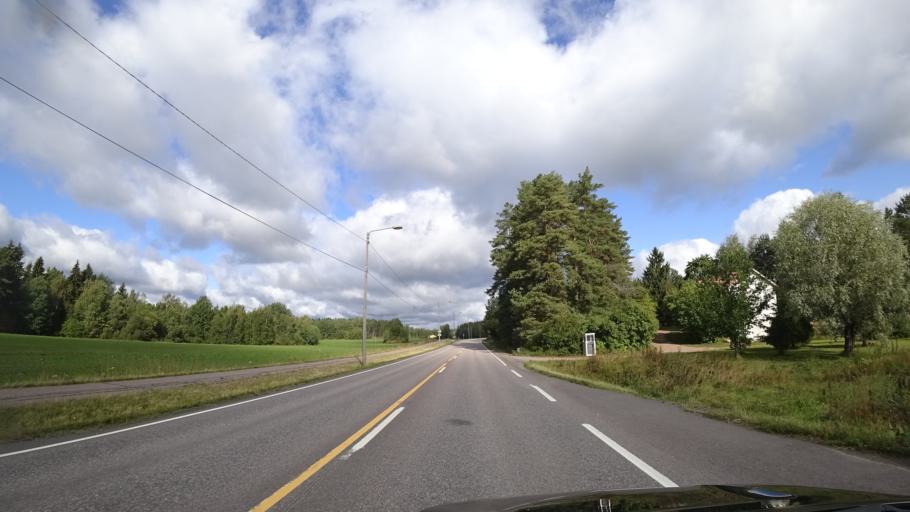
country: FI
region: Uusimaa
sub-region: Helsinki
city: Hyvinge
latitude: 60.6543
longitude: 24.9890
